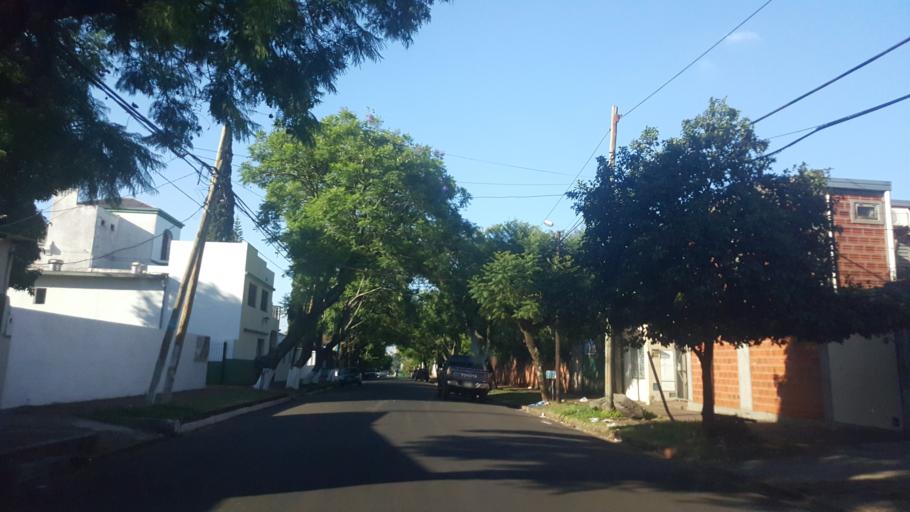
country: AR
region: Misiones
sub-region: Departamento de Capital
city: Posadas
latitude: -27.3866
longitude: -55.8946
